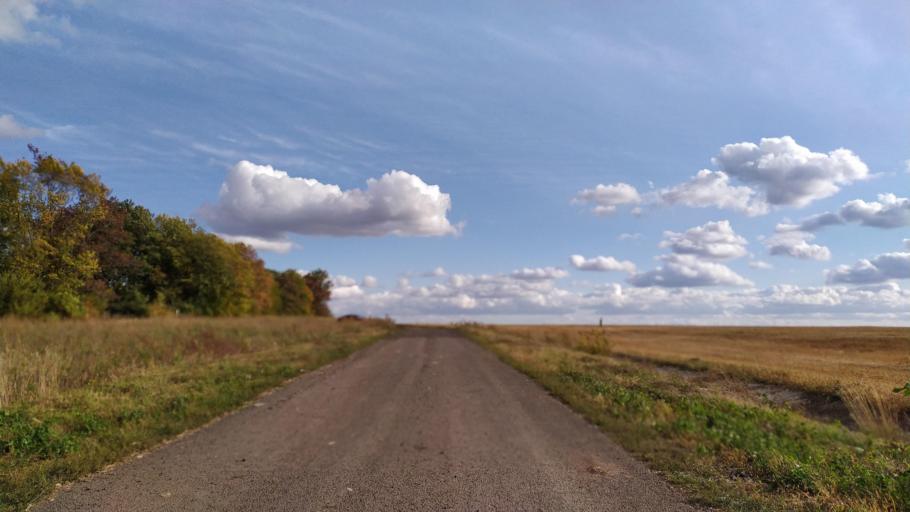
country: RU
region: Kursk
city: Kursk
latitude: 51.6137
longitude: 36.1644
